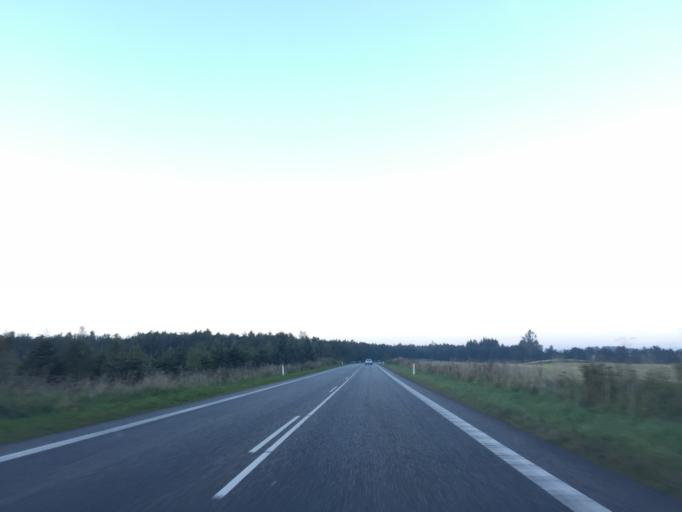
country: DK
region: South Denmark
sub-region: Aabenraa Kommune
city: Lojt Kirkeby
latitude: 55.0897
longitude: 9.4326
